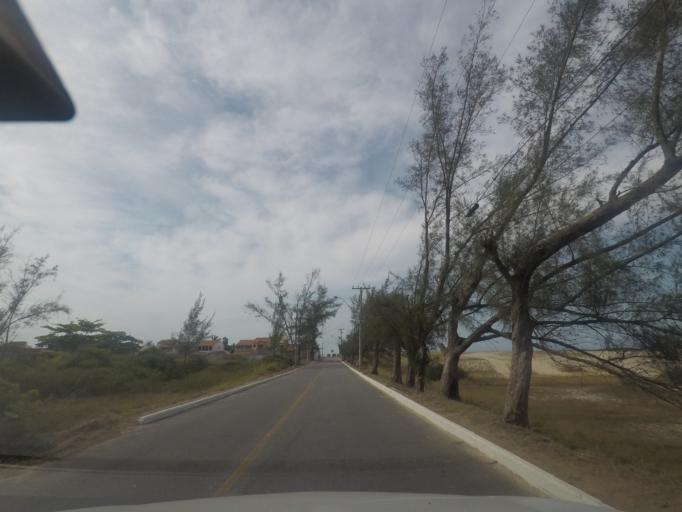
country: BR
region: Rio de Janeiro
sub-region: Marica
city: Marica
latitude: -22.9599
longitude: -42.8276
